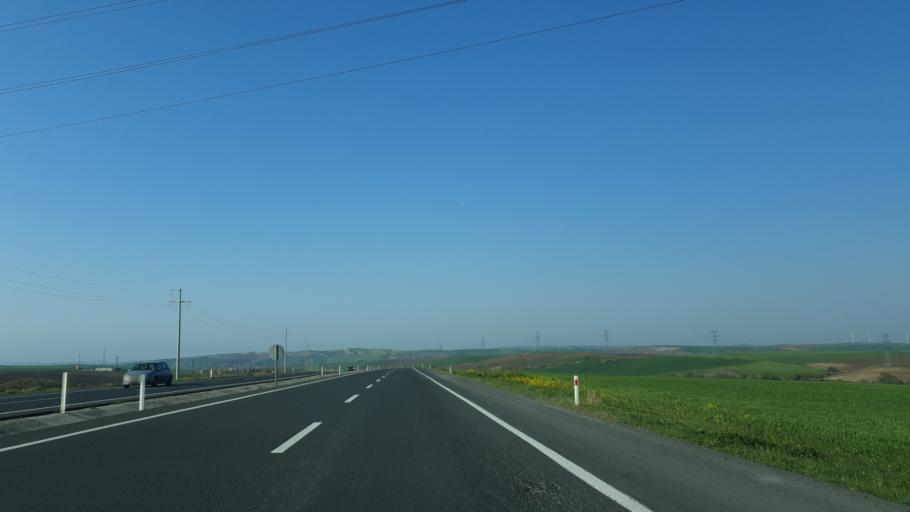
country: TR
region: Tekirdag
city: Corlu
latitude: 41.0974
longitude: 27.7523
